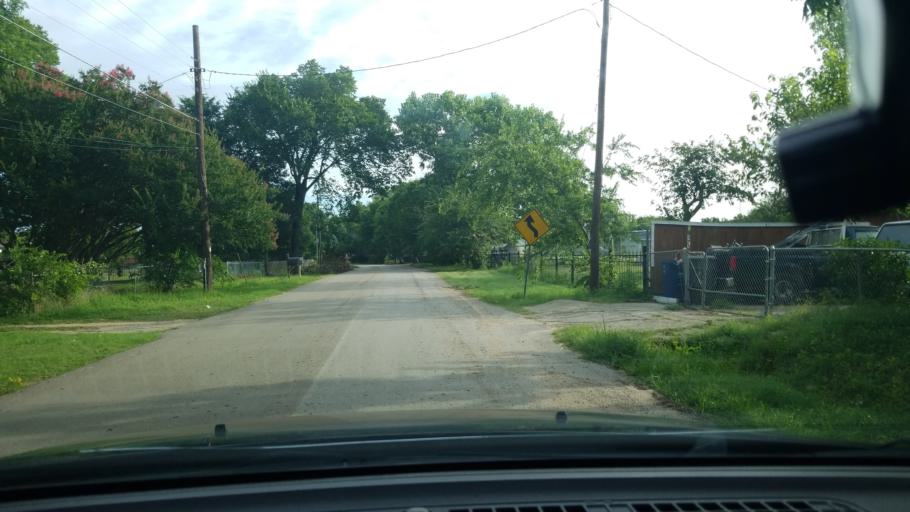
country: US
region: Texas
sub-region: Dallas County
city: Balch Springs
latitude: 32.7572
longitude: -96.6504
